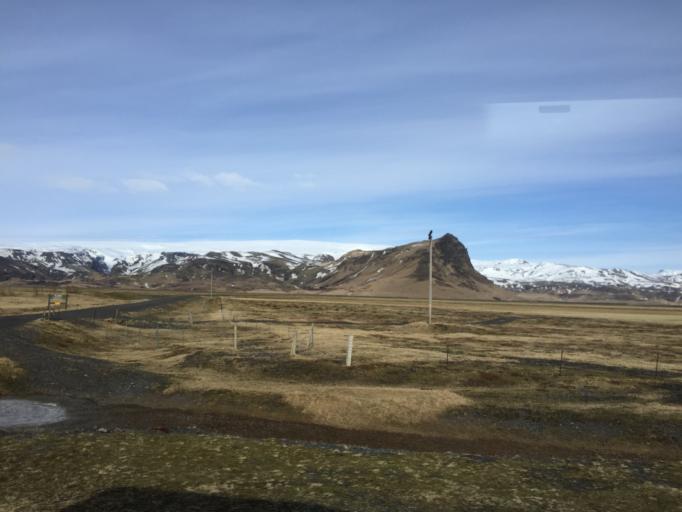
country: IS
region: South
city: Vestmannaeyjar
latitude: 63.4706
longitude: -19.2514
